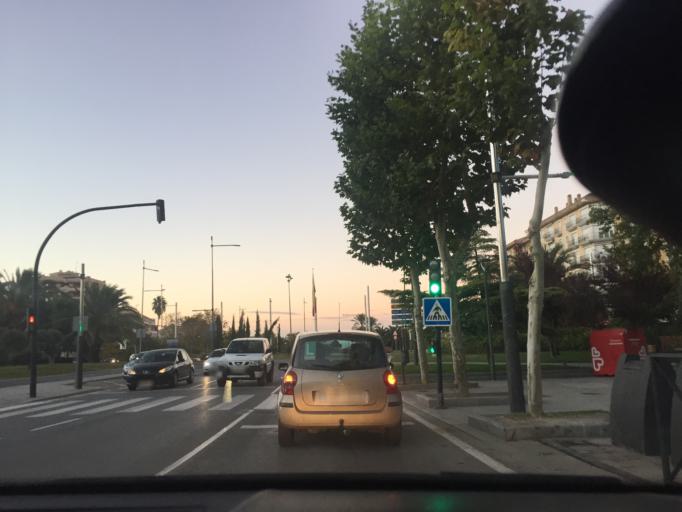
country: ES
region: Andalusia
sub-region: Provincia de Jaen
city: Jaen
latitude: 37.7794
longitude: -3.7896
